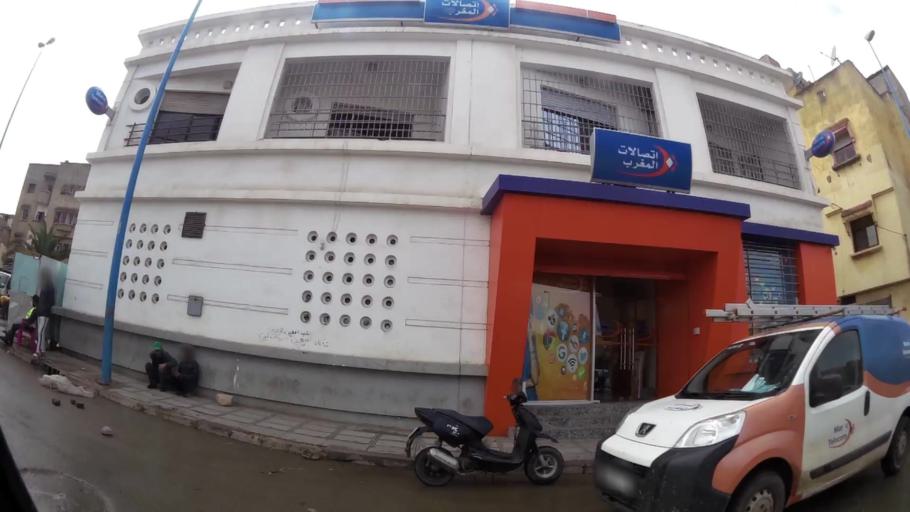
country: MA
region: Grand Casablanca
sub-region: Mohammedia
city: Mohammedia
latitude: 33.6395
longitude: -7.4508
